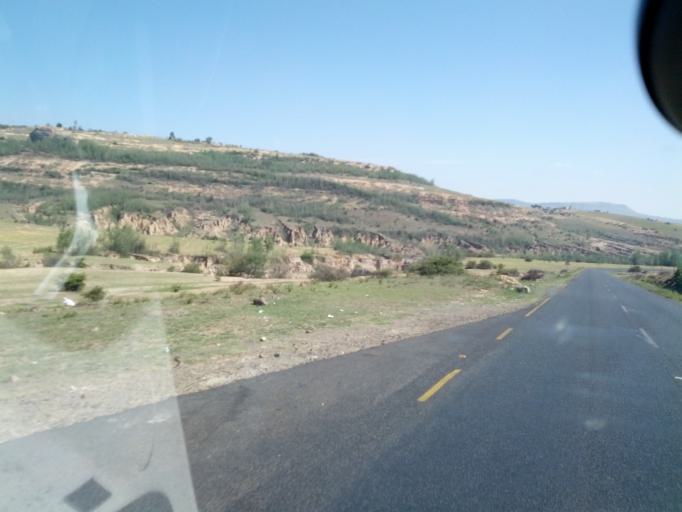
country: LS
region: Berea
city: Teyateyaneng
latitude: -29.1423
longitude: 27.7042
